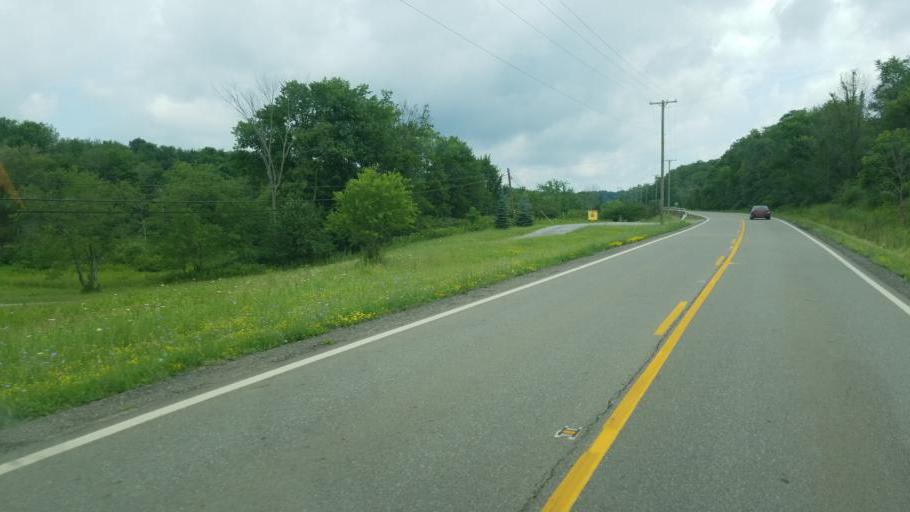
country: US
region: Ohio
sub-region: Columbiana County
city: Lisbon
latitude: 40.7357
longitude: -80.7894
